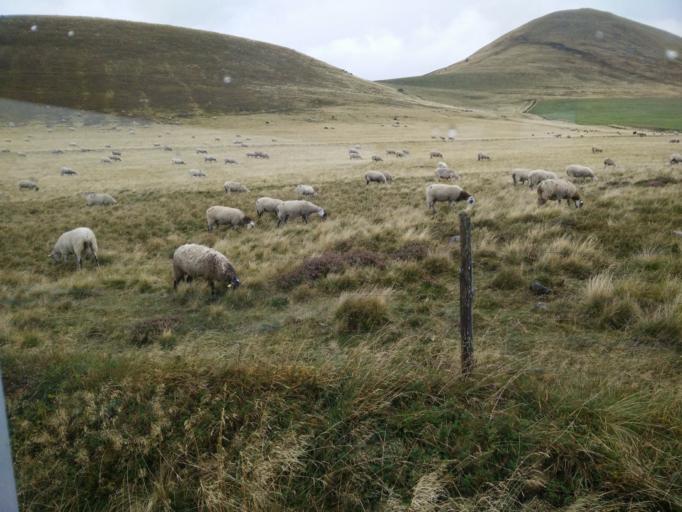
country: FR
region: Auvergne
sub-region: Departement du Puy-de-Dome
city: Mont-Dore
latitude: 45.5640
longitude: 2.8303
